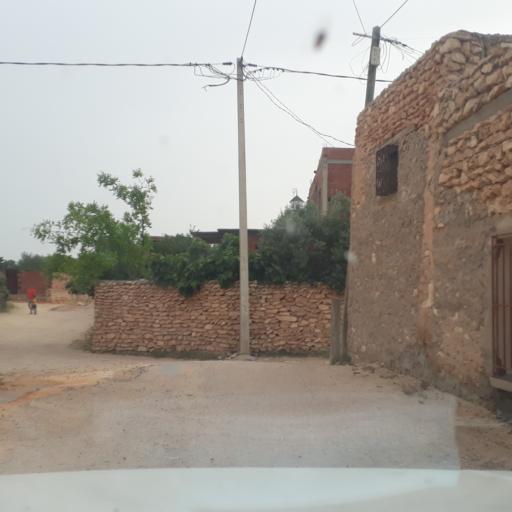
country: TN
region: Safaqis
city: Al Qarmadah
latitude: 34.8243
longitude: 10.7777
